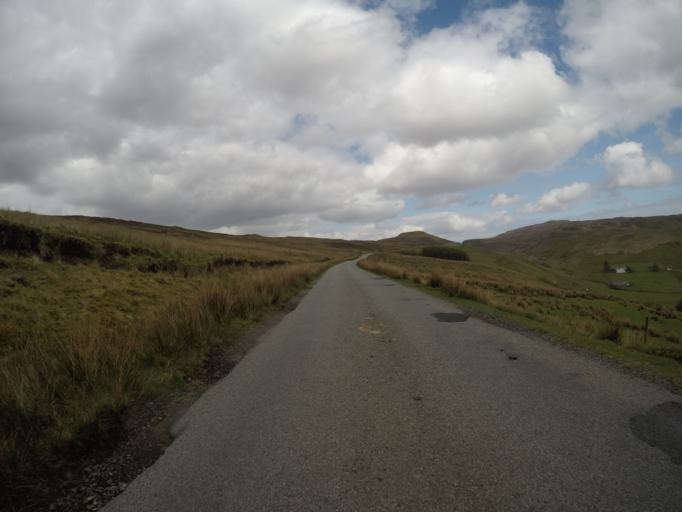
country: GB
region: Scotland
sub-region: Highland
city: Isle of Skye
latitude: 57.3691
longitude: -6.3828
